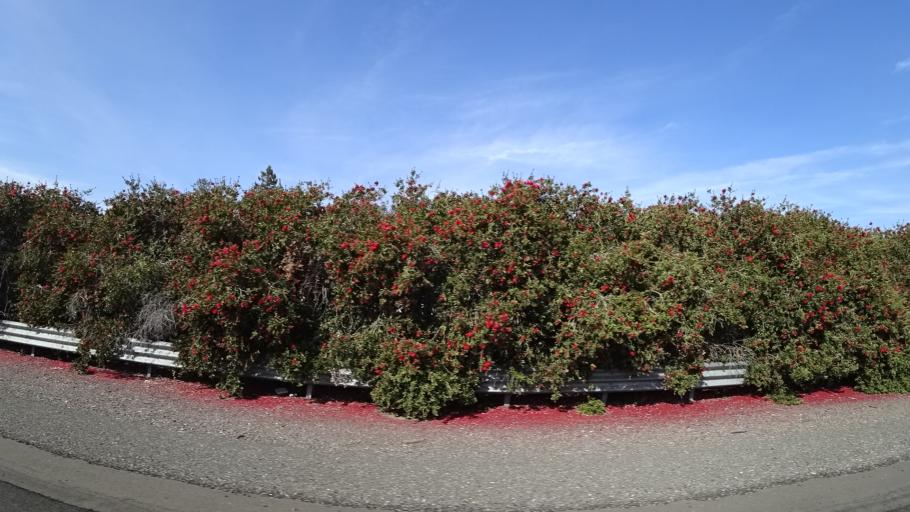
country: US
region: California
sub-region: Butte County
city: Chico
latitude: 39.7583
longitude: -121.8527
